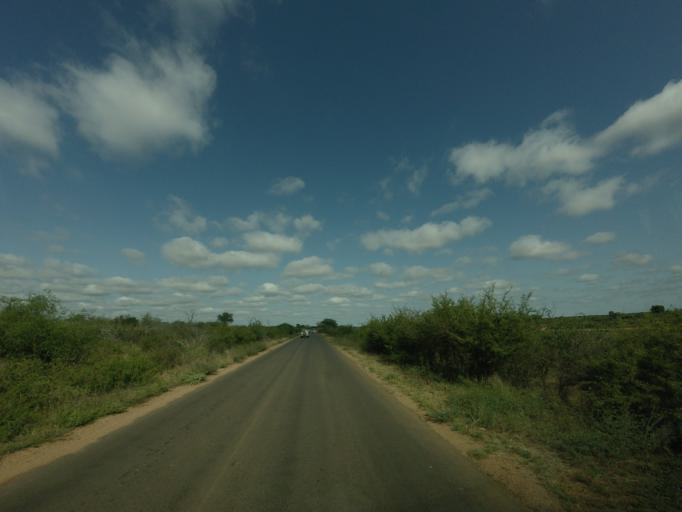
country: ZA
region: Mpumalanga
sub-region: Ehlanzeni District
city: Komatipoort
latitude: -25.1249
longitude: 31.9330
